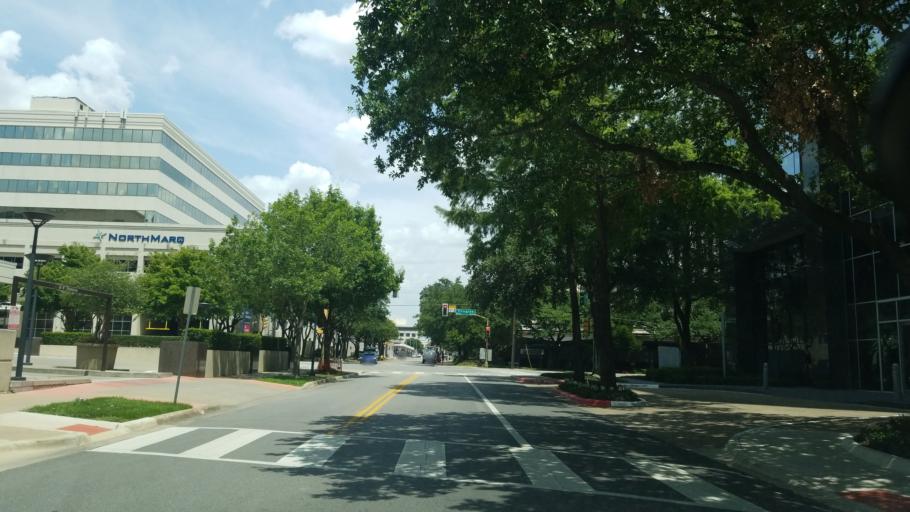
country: US
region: Texas
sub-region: Dallas County
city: University Park
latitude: 32.8636
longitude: -96.8093
